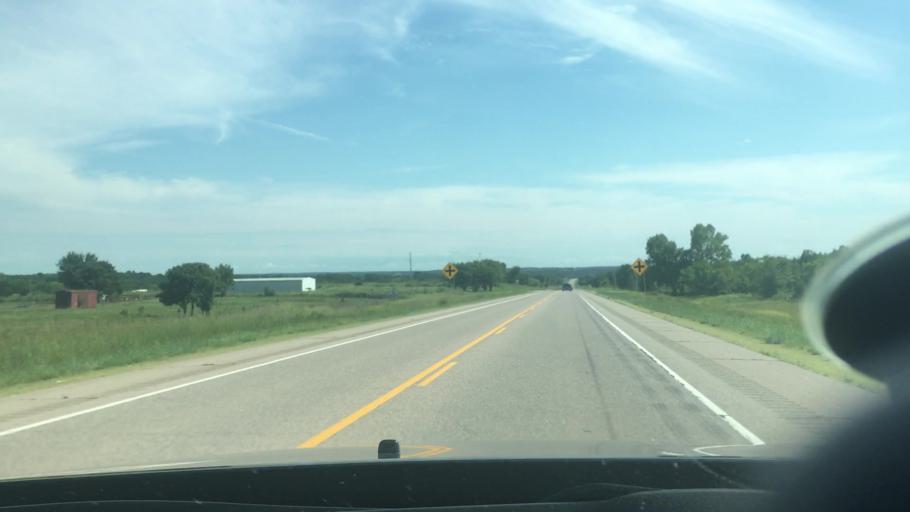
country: US
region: Oklahoma
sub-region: Seminole County
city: Maud
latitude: 35.0894
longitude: -96.6788
